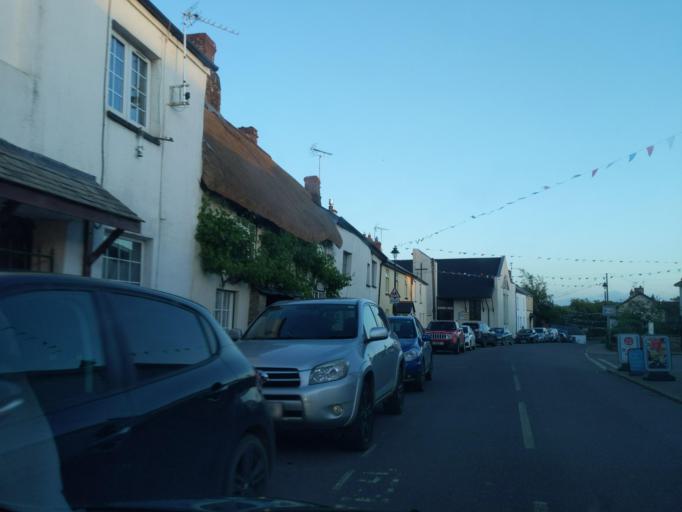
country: GB
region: England
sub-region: Devon
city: Okehampton
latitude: 50.8205
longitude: -4.0724
